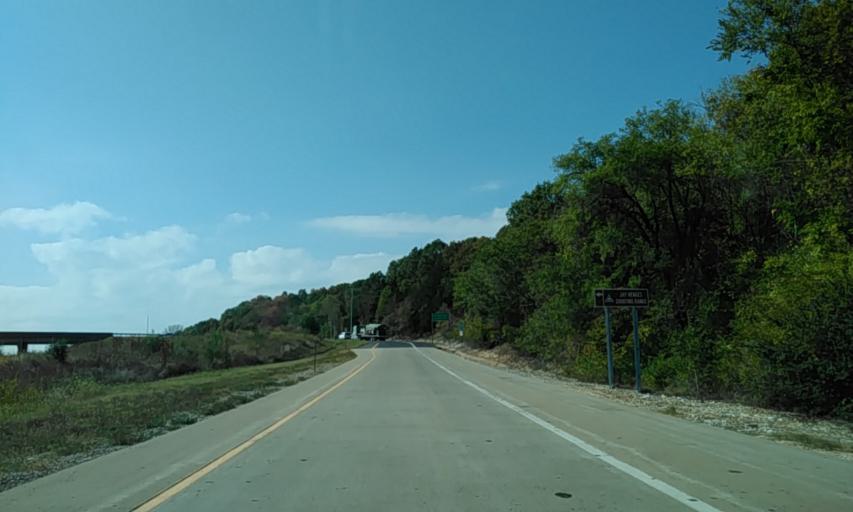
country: US
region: Missouri
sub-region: Jefferson County
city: High Ridge
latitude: 38.5170
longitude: -90.5490
